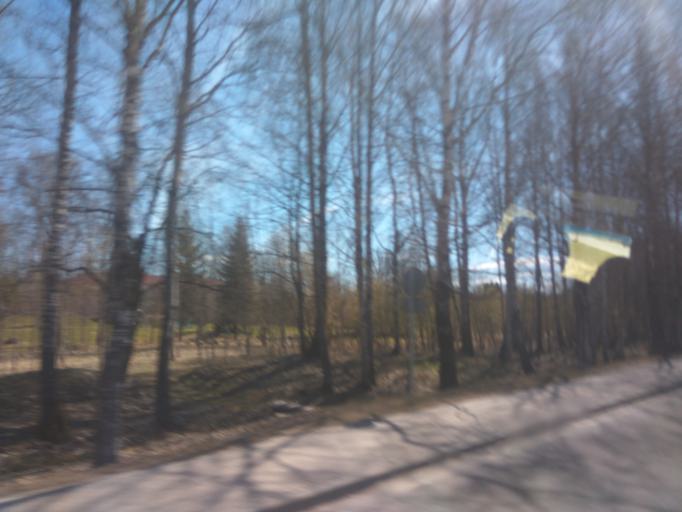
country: LV
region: Aluksnes Rajons
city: Aluksne
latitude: 57.4338
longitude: 27.0390
